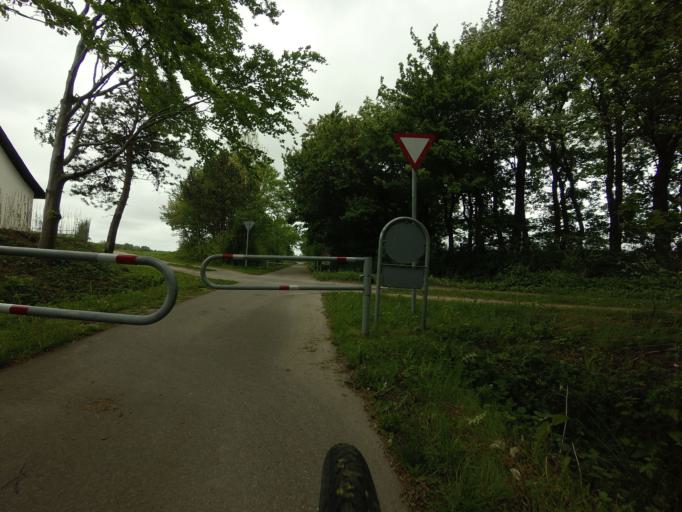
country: DK
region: Zealand
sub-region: Slagelse Kommune
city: Slagelse
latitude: 55.3490
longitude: 11.3932
